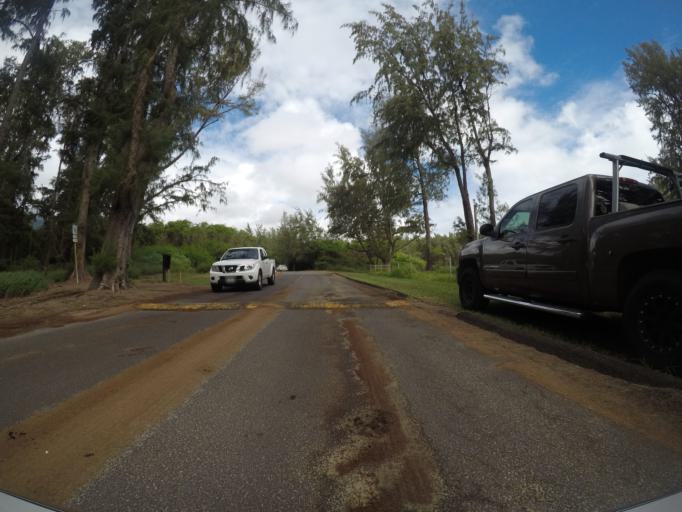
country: US
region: Hawaii
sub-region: Honolulu County
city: Waimanalo Beach
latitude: 21.3443
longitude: -157.7035
